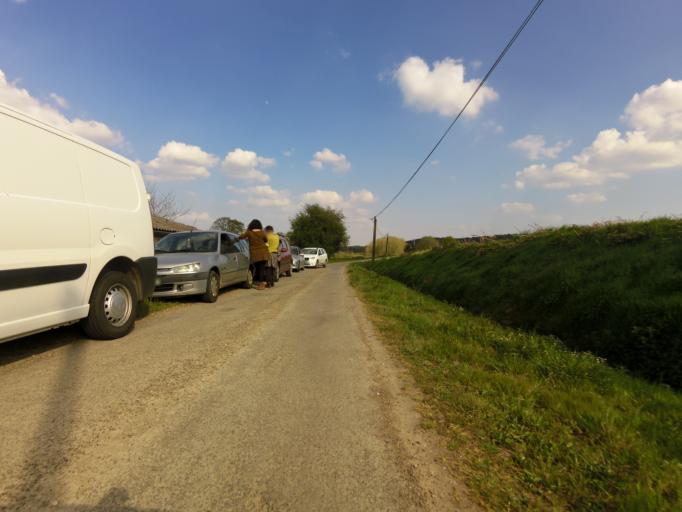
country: FR
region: Brittany
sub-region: Departement du Morbihan
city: Pluherlin
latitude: 47.7111
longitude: -2.3434
